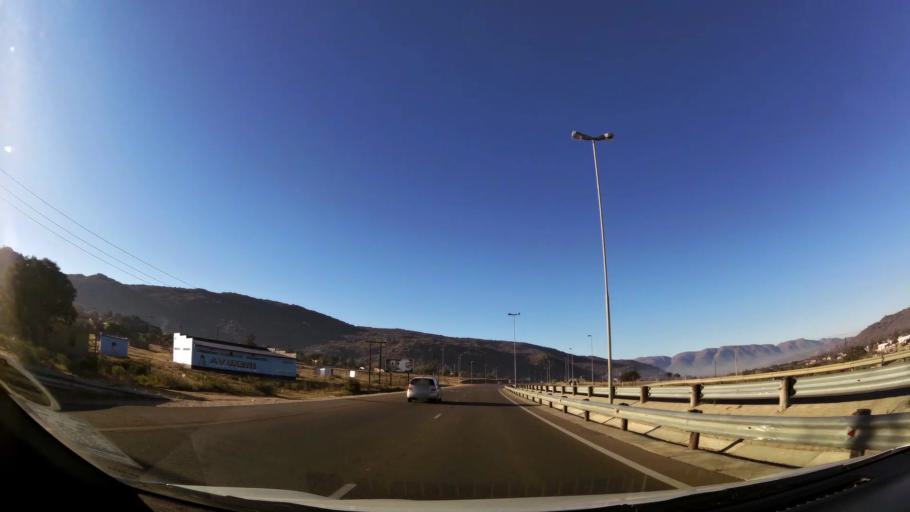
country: ZA
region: Limpopo
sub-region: Capricorn District Municipality
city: Mankoeng
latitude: -23.9185
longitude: 29.7926
